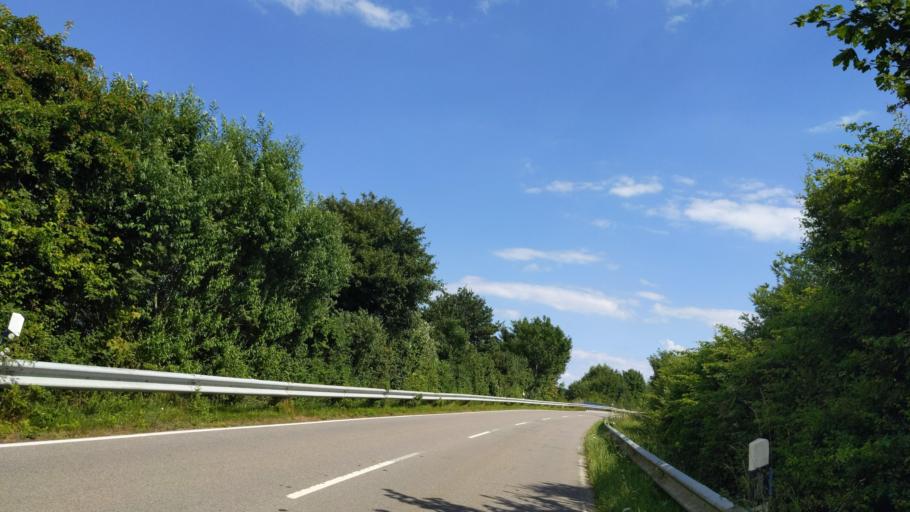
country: DE
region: Schleswig-Holstein
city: Manhagen
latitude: 54.1609
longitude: 10.9141
